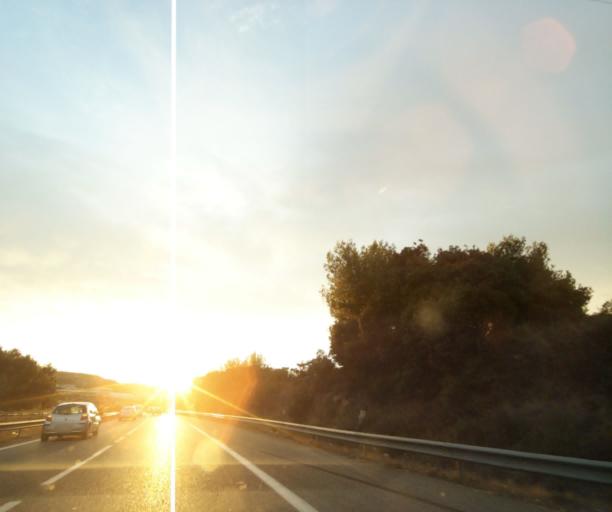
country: FR
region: Provence-Alpes-Cote d'Azur
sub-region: Departement des Bouches-du-Rhone
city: Gignac-la-Nerthe
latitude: 43.3840
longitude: 5.2294
